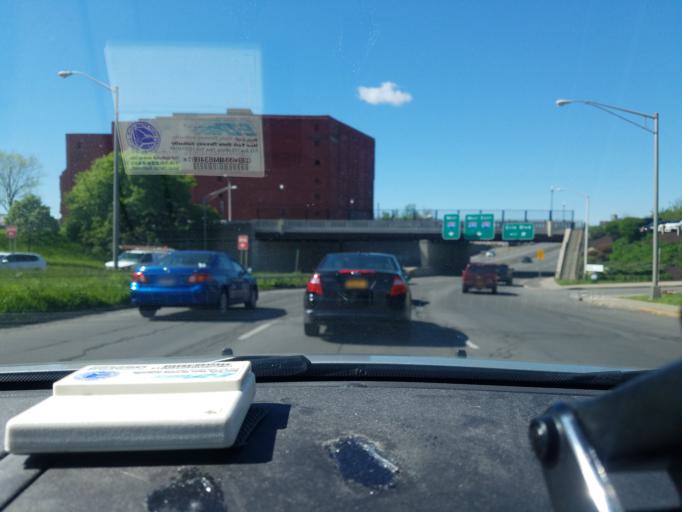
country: US
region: New York
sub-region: Onondaga County
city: Syracuse
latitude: 43.0497
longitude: -76.1588
